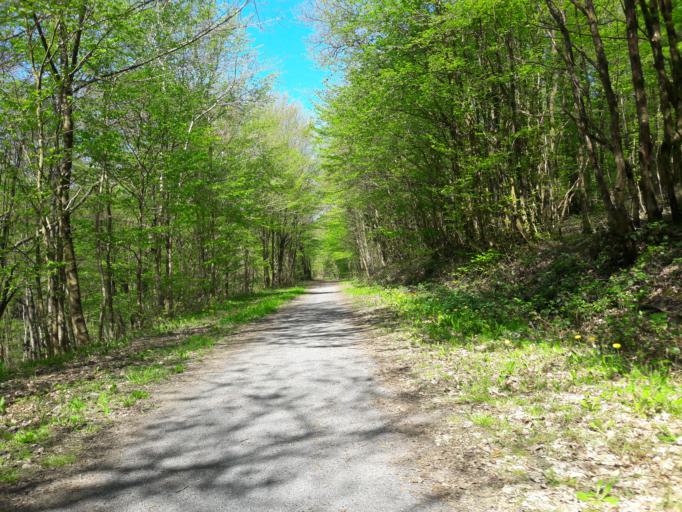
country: FR
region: Nord-Pas-de-Calais
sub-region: Departement du Nord
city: Sains-du-Nord
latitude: 50.1296
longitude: 4.0658
